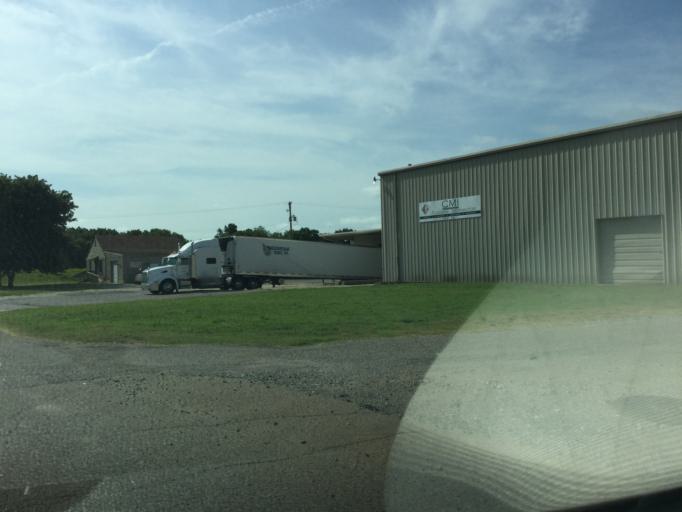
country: US
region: Kansas
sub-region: Shawnee County
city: Topeka
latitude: 39.0466
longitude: -95.6661
